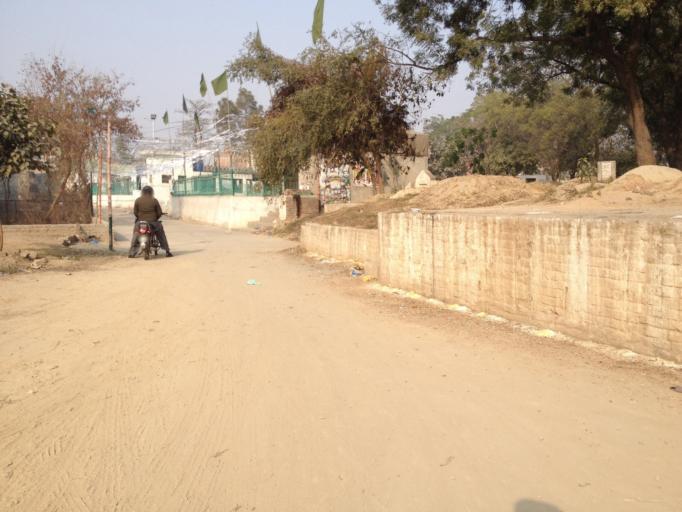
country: PK
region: Punjab
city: Lahore
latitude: 31.5773
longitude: 74.4152
